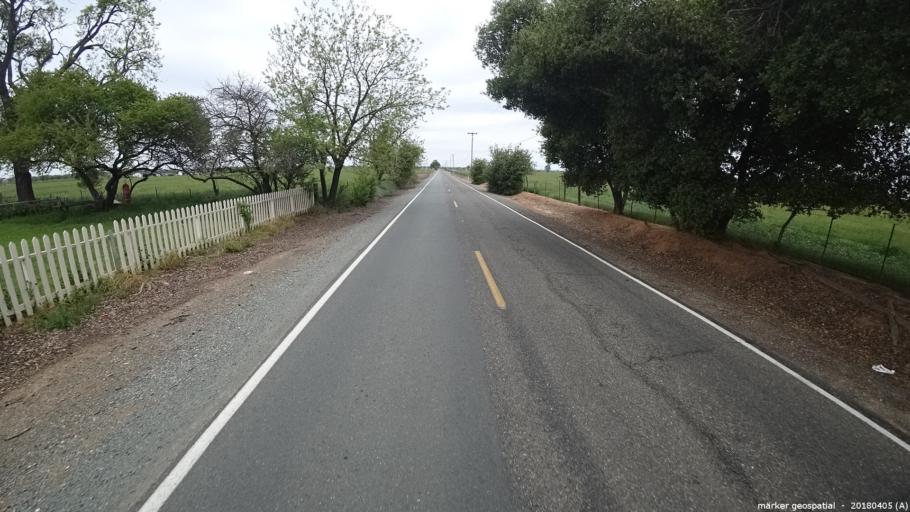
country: US
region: California
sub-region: Sacramento County
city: Galt
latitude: 38.2473
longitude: -121.3486
